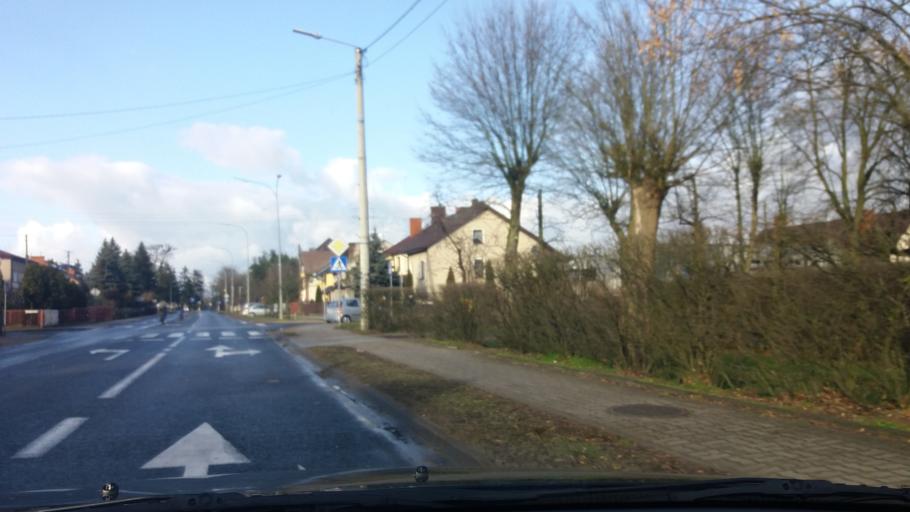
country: PL
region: Masovian Voivodeship
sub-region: Powiat przasnyski
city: Chorzele
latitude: 53.2644
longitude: 20.8974
